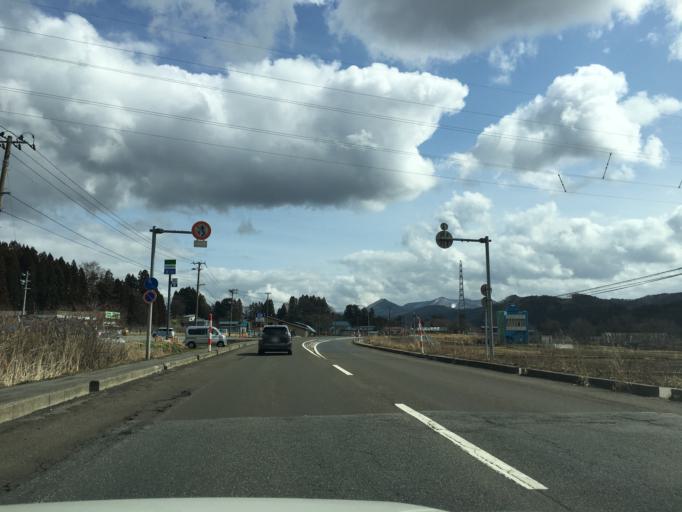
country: JP
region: Akita
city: Odate
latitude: 40.2285
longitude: 140.5972
